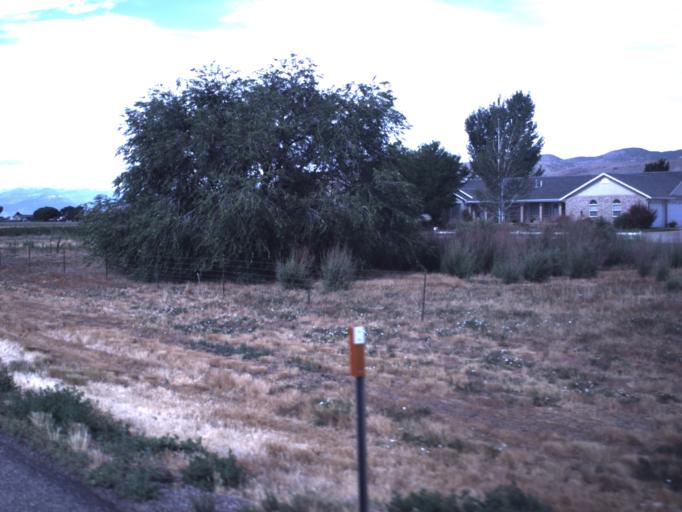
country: US
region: Utah
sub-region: Sevier County
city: Richfield
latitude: 38.7269
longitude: -112.0989
